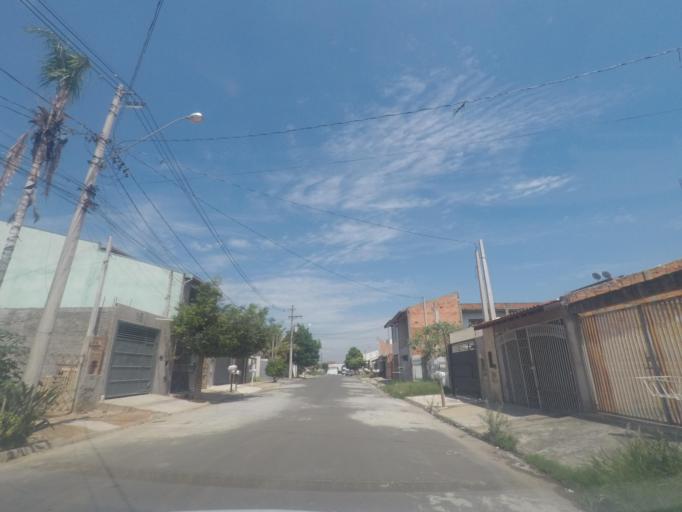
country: BR
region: Sao Paulo
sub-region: Sumare
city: Sumare
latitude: -22.8018
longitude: -47.2660
